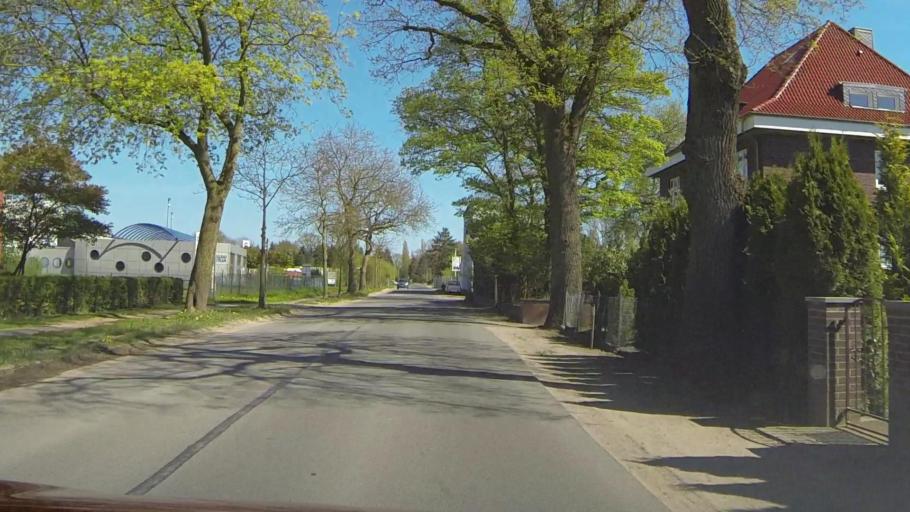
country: DE
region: Schleswig-Holstein
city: Moorrege
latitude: 53.6780
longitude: 9.6947
